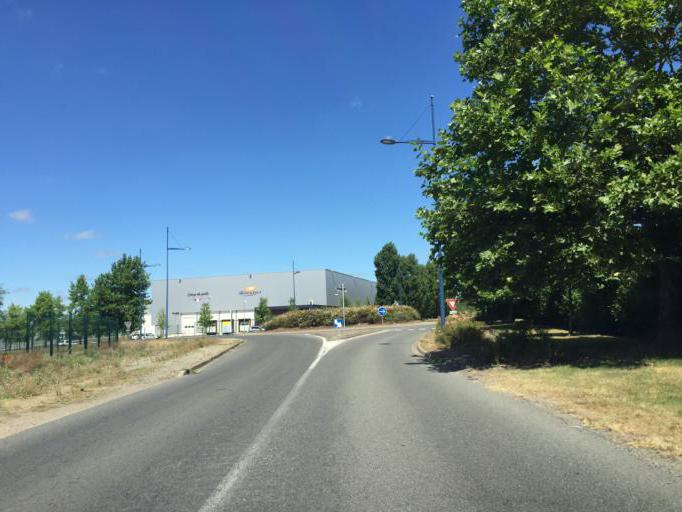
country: FR
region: Auvergne
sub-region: Departement de l'Allier
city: Moulins
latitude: 46.5928
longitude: 3.3317
